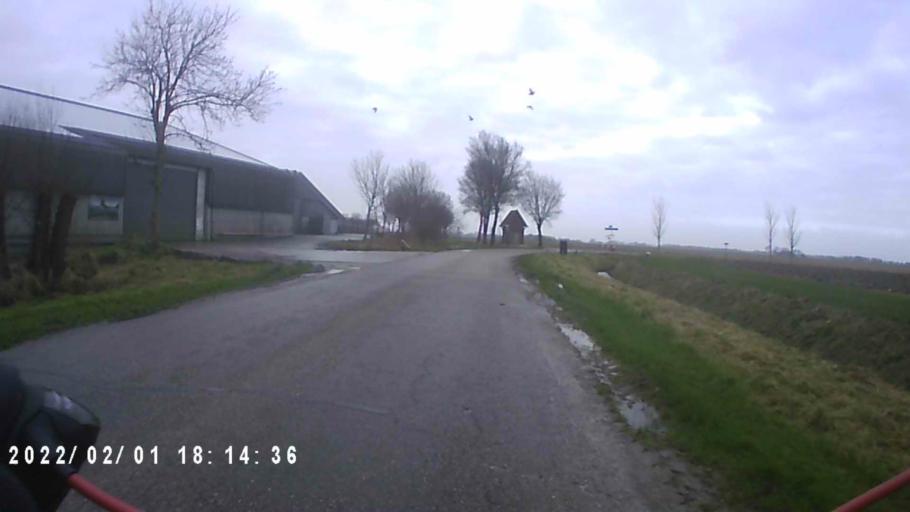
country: NL
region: Groningen
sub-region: Gemeente De Marne
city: Ulrum
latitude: 53.3478
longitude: 6.3364
